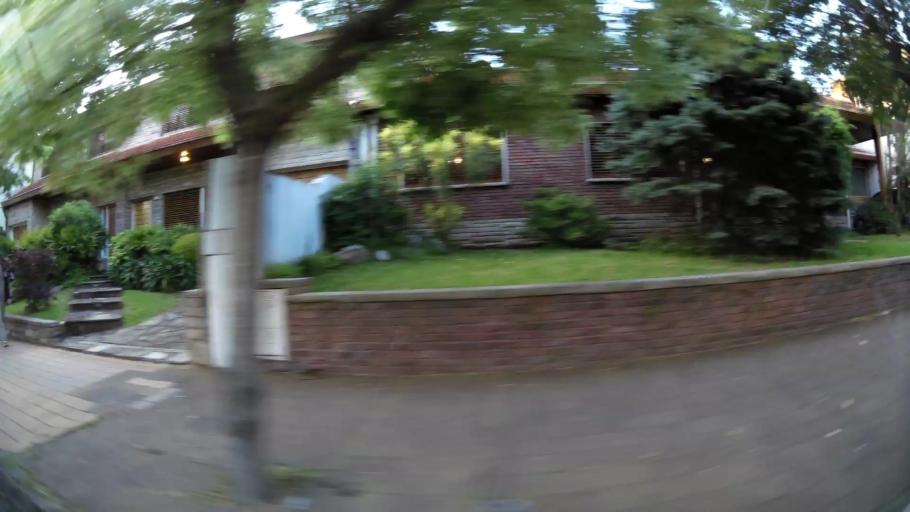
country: AR
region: Buenos Aires
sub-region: Partido de Vicente Lopez
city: Olivos
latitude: -34.5393
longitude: -58.5012
